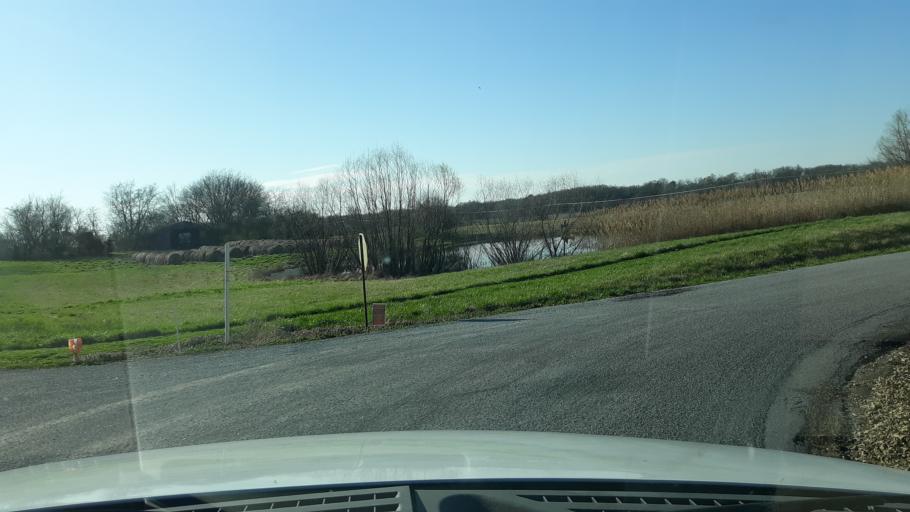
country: US
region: Illinois
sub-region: Saline County
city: Harrisburg
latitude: 37.7645
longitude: -88.5863
